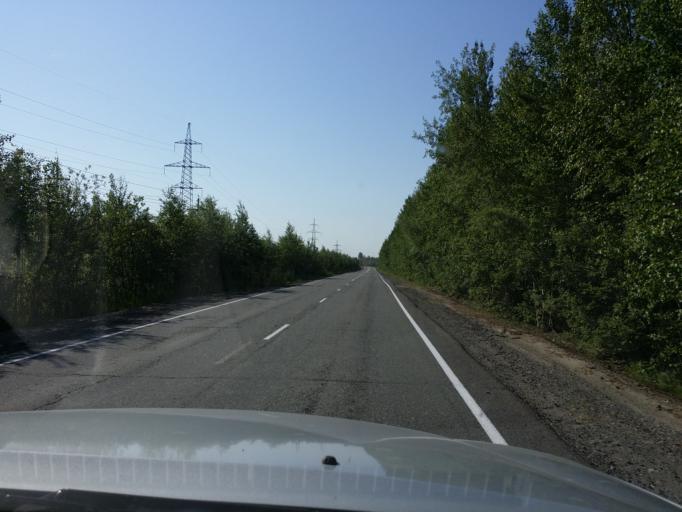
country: RU
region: Khanty-Mansiyskiy Avtonomnyy Okrug
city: Izluchinsk
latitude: 60.8919
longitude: 77.0684
